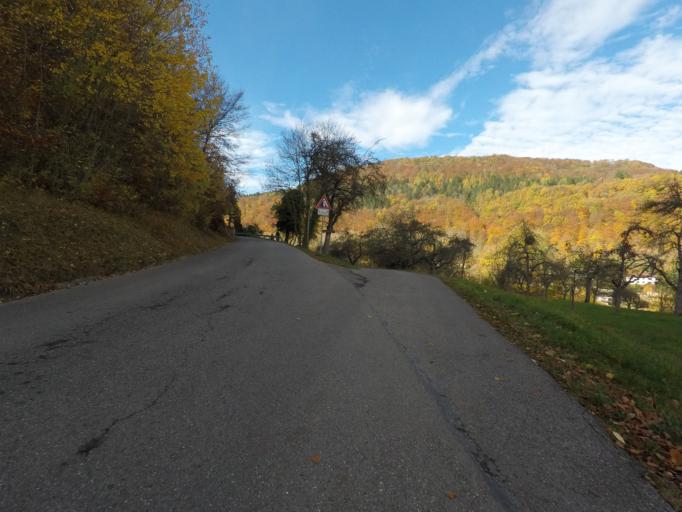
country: DE
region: Baden-Wuerttemberg
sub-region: Tuebingen Region
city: Pfullingen
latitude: 48.4251
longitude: 9.2502
